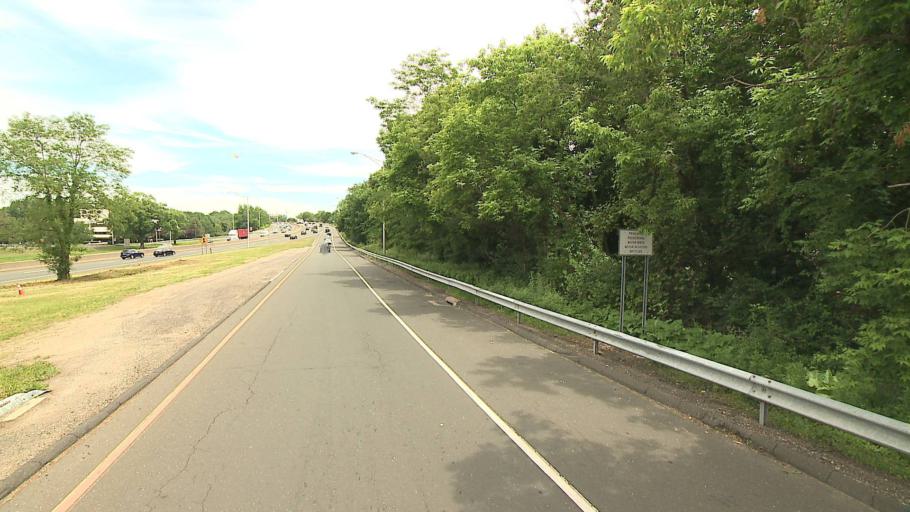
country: US
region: Connecticut
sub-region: Fairfield County
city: Cos Cob
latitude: 41.0262
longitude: -73.6053
